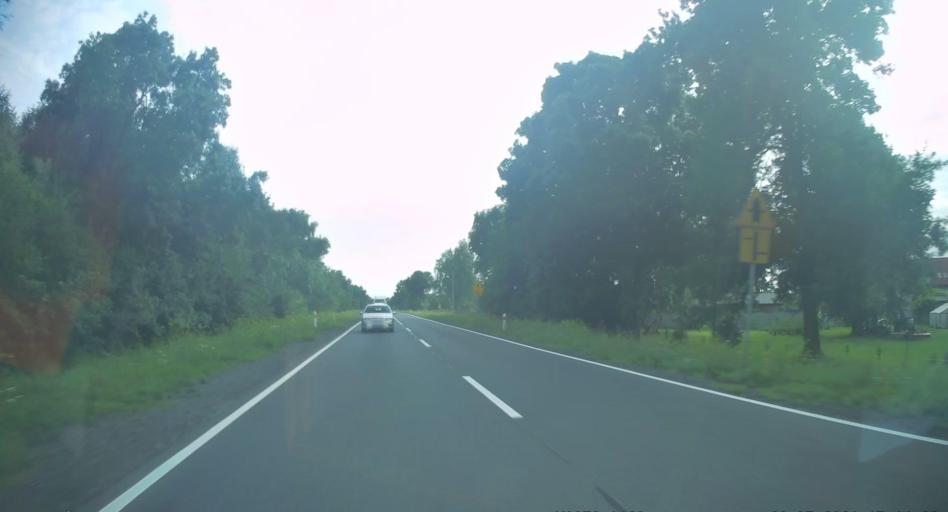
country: PL
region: Silesian Voivodeship
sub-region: Powiat czestochowski
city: Klomnice
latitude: 50.9376
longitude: 19.3864
